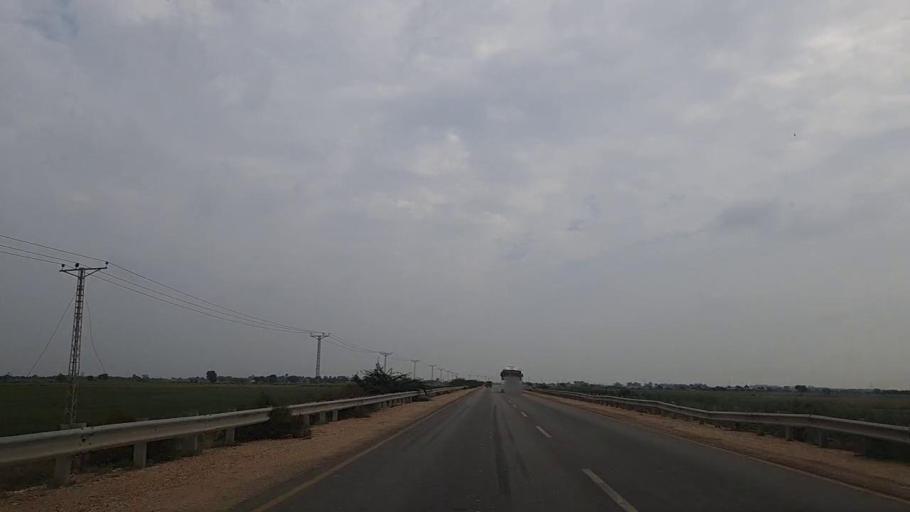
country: PK
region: Sindh
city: Thatta
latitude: 24.6174
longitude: 68.0694
